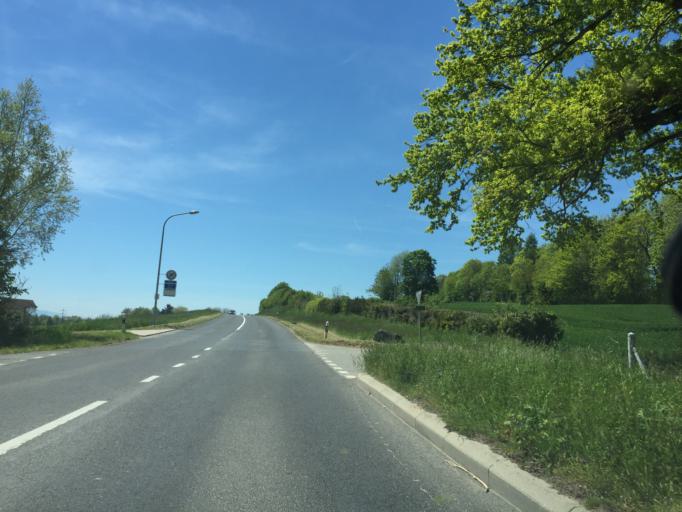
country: CH
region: Vaud
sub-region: Morges District
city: Apples
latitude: 46.5275
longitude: 6.4398
